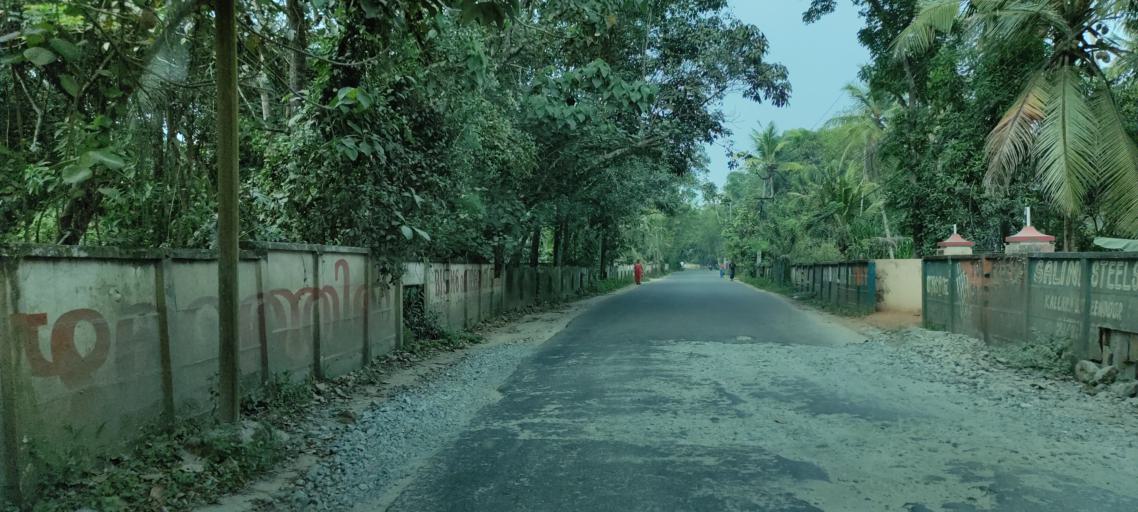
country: IN
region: Kerala
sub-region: Kottayam
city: Vaikam
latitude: 9.7197
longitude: 76.4164
